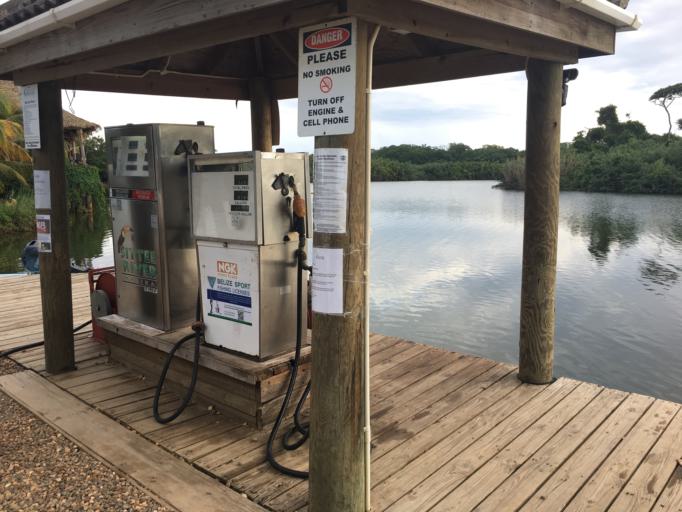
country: BZ
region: Stann Creek
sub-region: Dangriga
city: Dangriga
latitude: 16.8218
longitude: -88.2685
